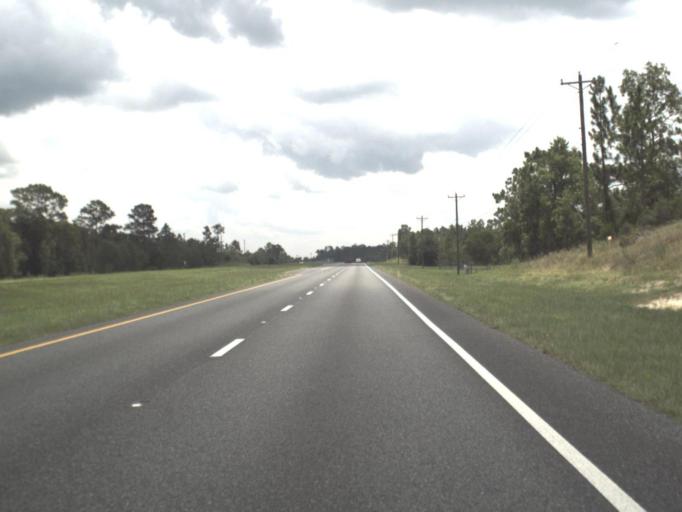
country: US
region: Florida
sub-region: Levy County
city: East Bronson
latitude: 29.4319
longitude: -82.6070
